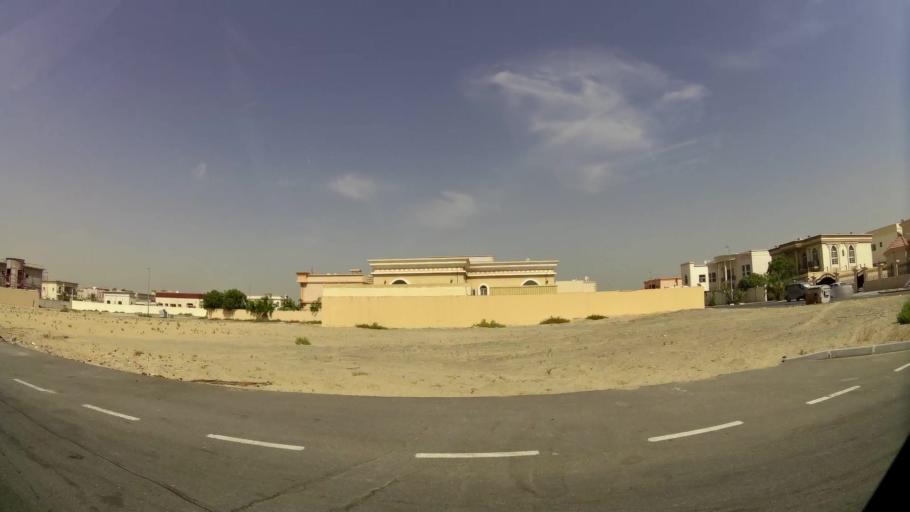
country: AE
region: Ash Shariqah
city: Sharjah
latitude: 25.2030
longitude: 55.4154
